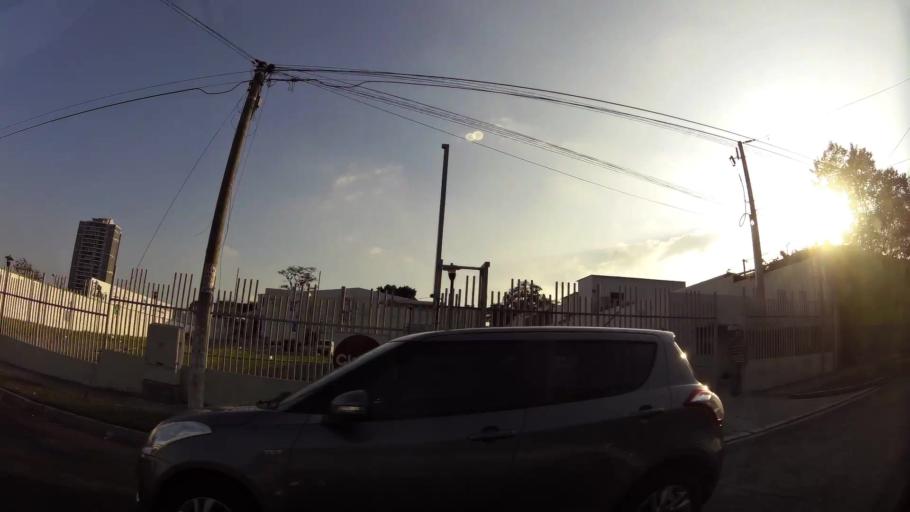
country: SV
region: La Libertad
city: Antiguo Cuscatlan
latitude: 13.6978
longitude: -89.2390
